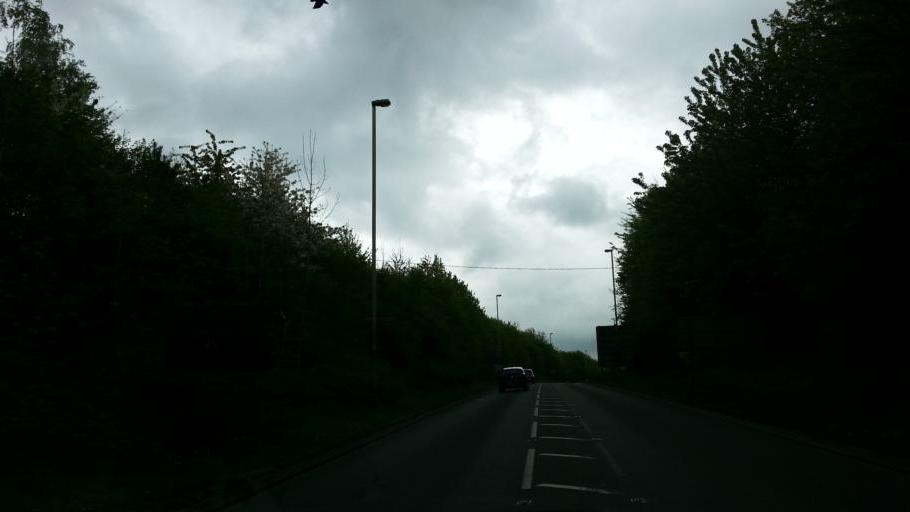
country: GB
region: England
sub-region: Leicestershire
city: Lutterworth
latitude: 52.4497
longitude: -1.1979
